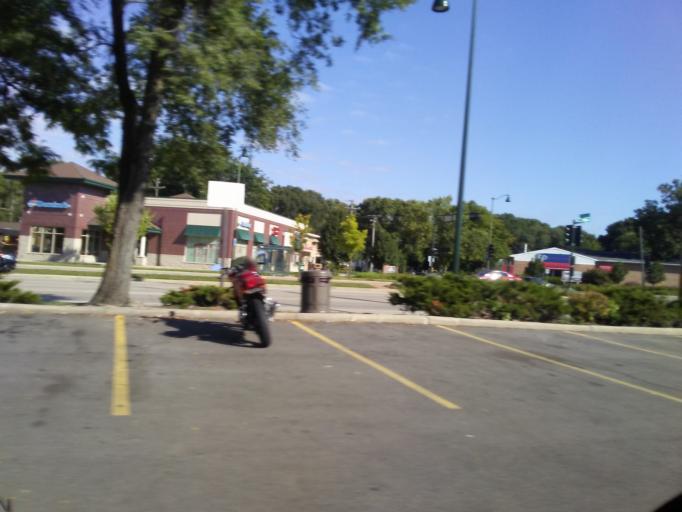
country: US
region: Wisconsin
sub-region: Dane County
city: Maple Bluff
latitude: 43.1024
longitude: -89.3454
